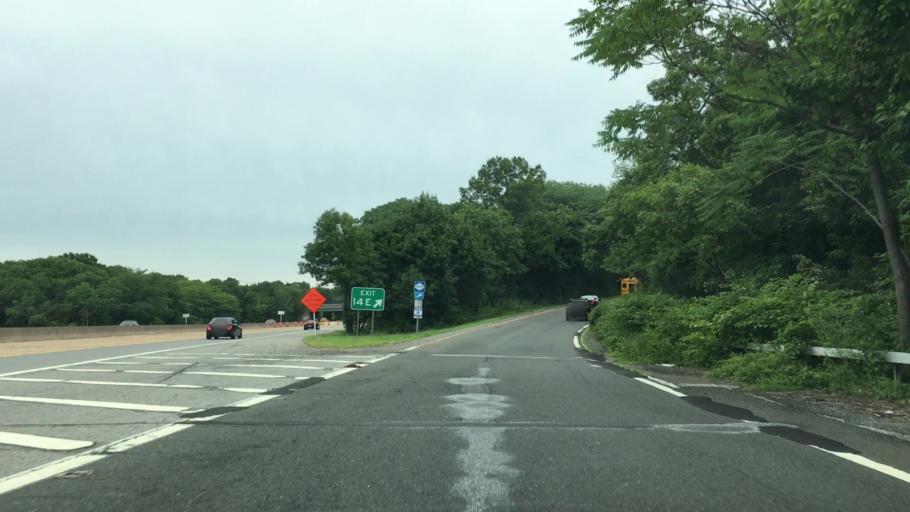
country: US
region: New York
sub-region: Nassau County
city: Syosset
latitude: 40.8088
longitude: -73.4913
